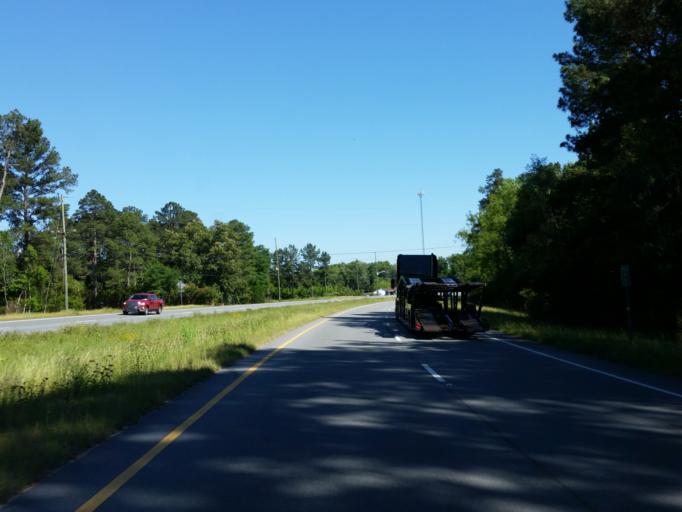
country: US
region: Georgia
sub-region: Lowndes County
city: Valdosta
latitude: 30.7638
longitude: -83.2225
